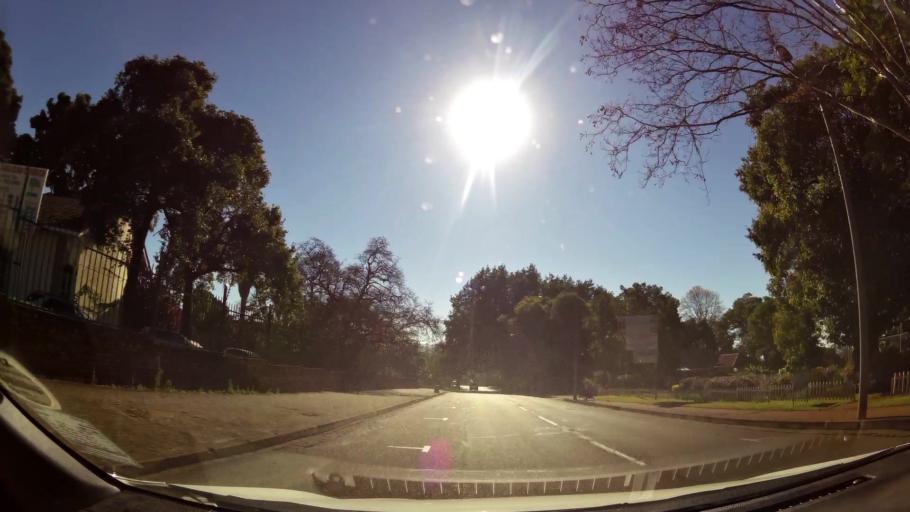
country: ZA
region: Limpopo
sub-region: Mopani District Municipality
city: Tzaneen
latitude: -23.8311
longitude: 30.1568
